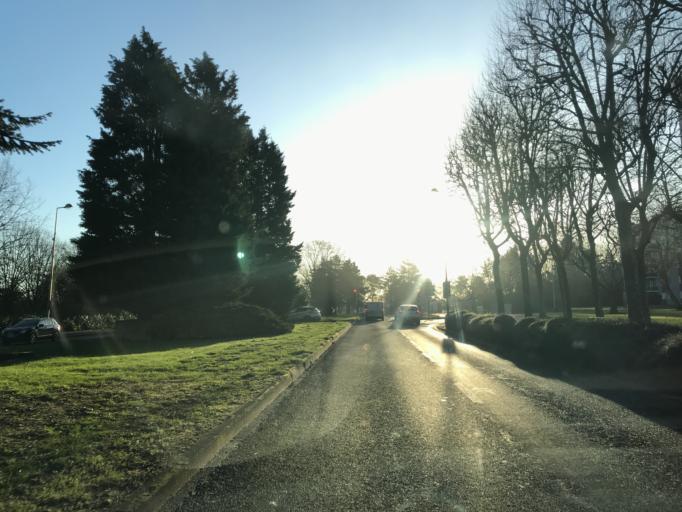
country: FR
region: Haute-Normandie
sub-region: Departement de la Seine-Maritime
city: Le Grand-Quevilly
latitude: 49.4059
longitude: 1.0522
